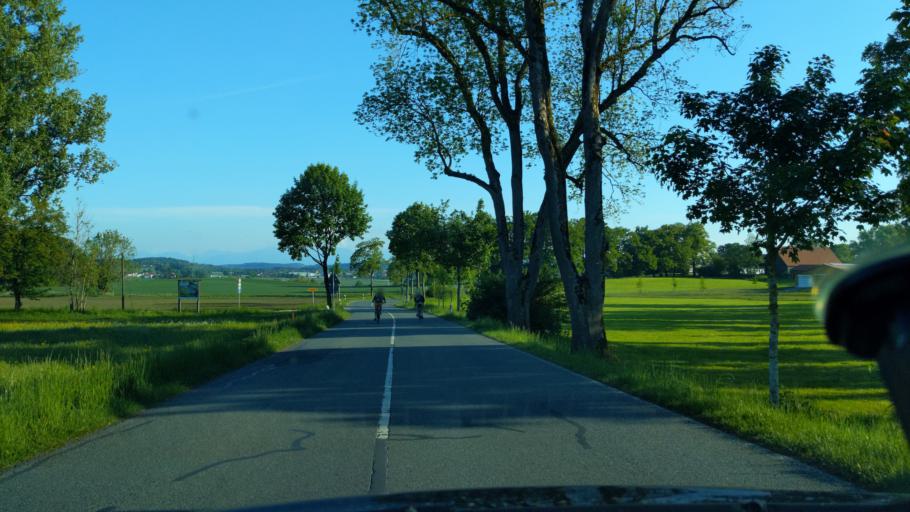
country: DE
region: Bavaria
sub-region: Upper Bavaria
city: Ebersberg
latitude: 48.0696
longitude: 11.9693
